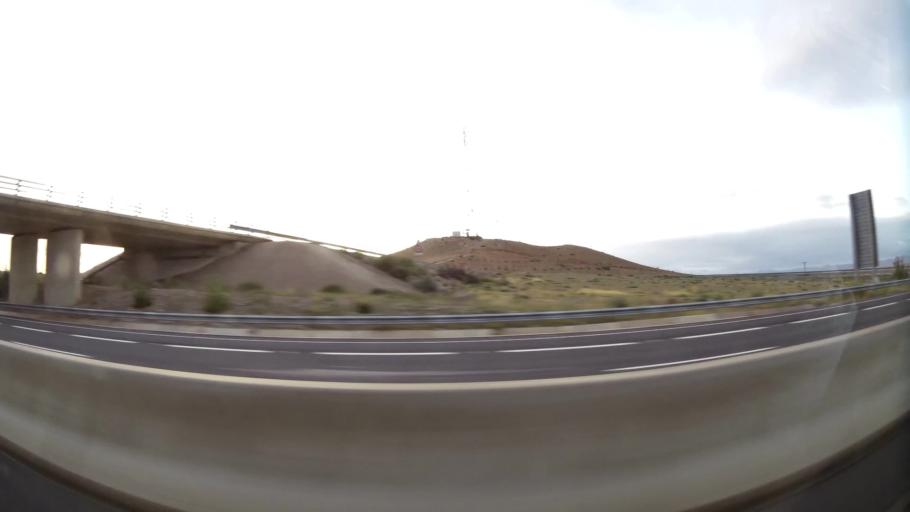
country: MA
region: Oriental
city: Taourirt
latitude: 34.5244
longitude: -2.9313
